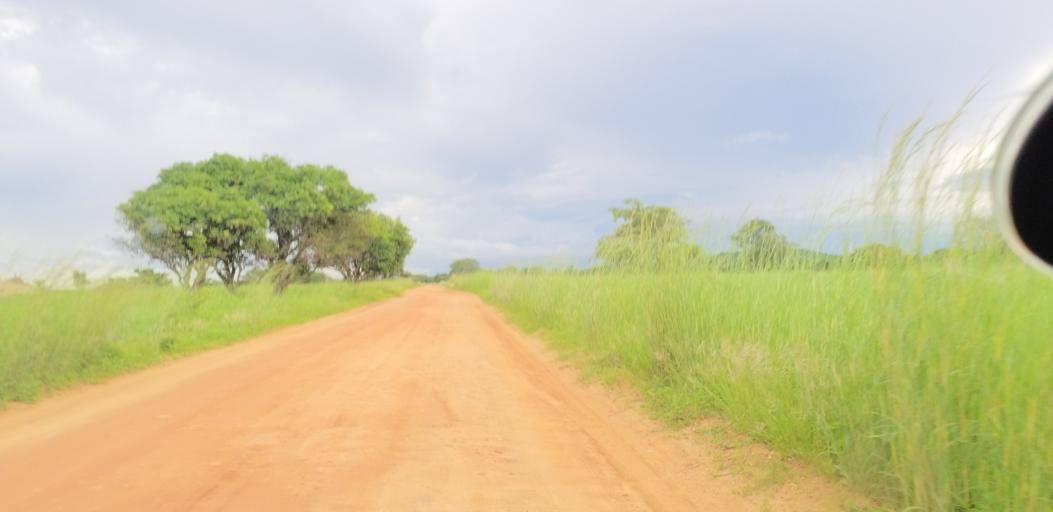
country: ZM
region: Lusaka
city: Chongwe
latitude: -15.1723
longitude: 28.4690
